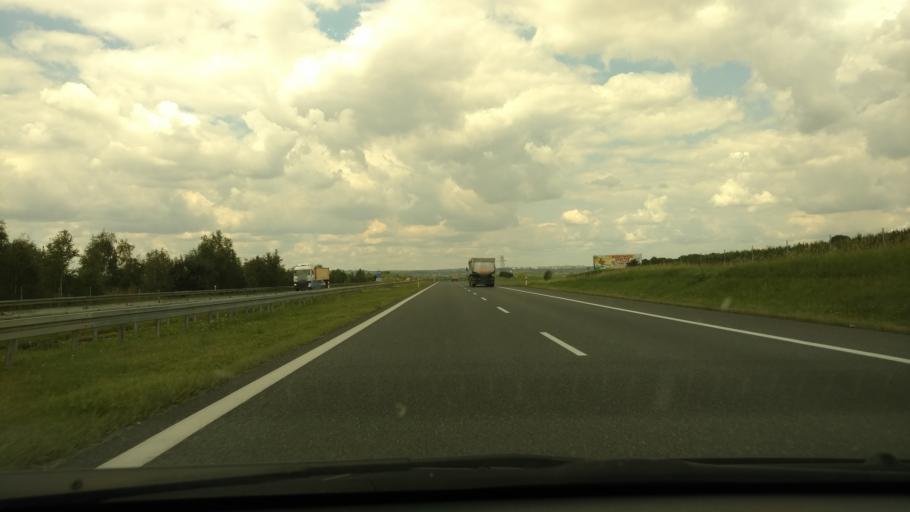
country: PL
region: Silesian Voivodeship
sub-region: Powiat bierunsko-ledzinski
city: Imielin
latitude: 50.1712
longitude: 19.2115
